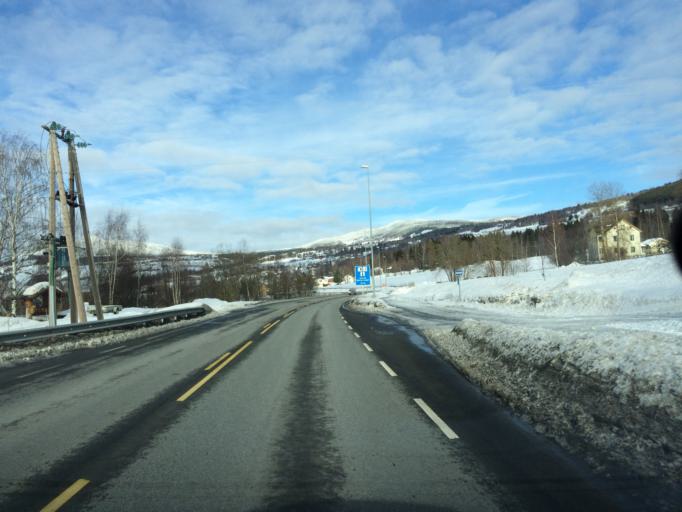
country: NO
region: Oppland
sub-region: Gausdal
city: Segalstad bru
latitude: 61.2075
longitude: 10.2987
